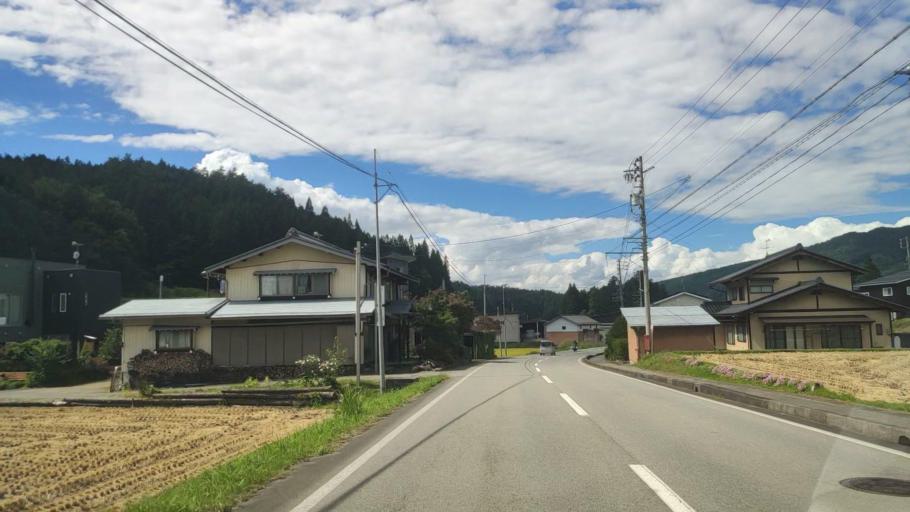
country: JP
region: Gifu
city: Takayama
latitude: 36.1722
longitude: 137.2963
